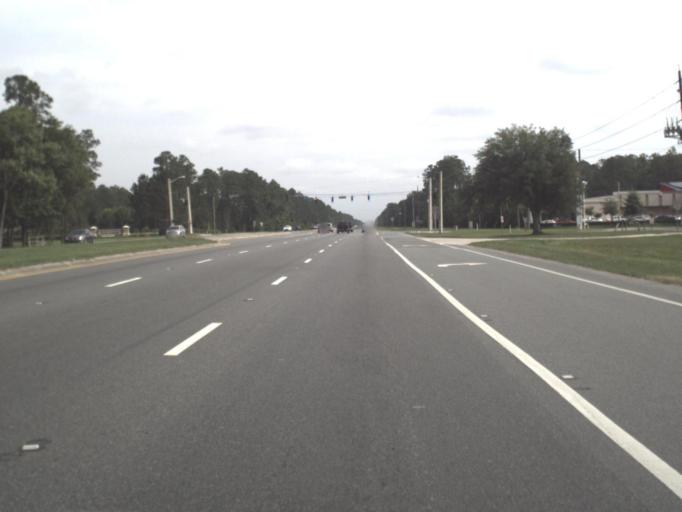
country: US
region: Florida
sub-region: Saint Johns County
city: Fruit Cove
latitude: 30.0674
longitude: -81.7073
